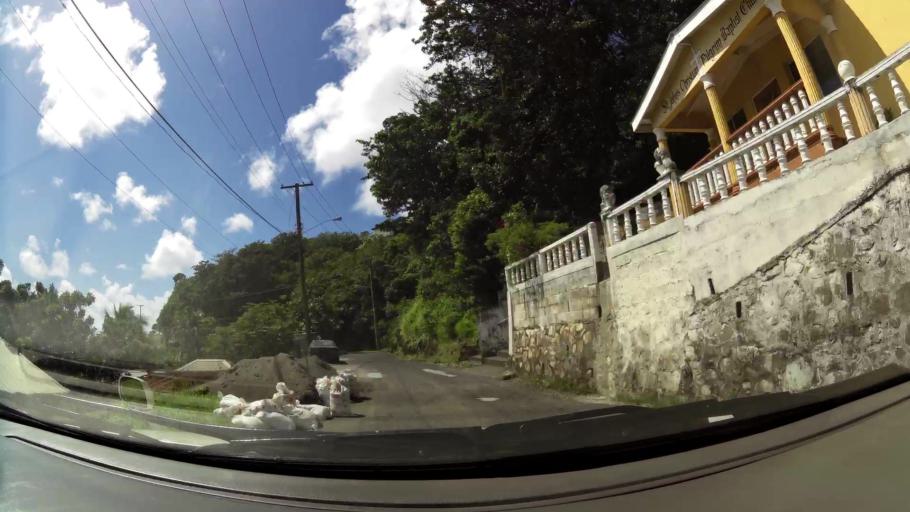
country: VC
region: Saint George
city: Kingstown
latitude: 13.1486
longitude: -61.2194
